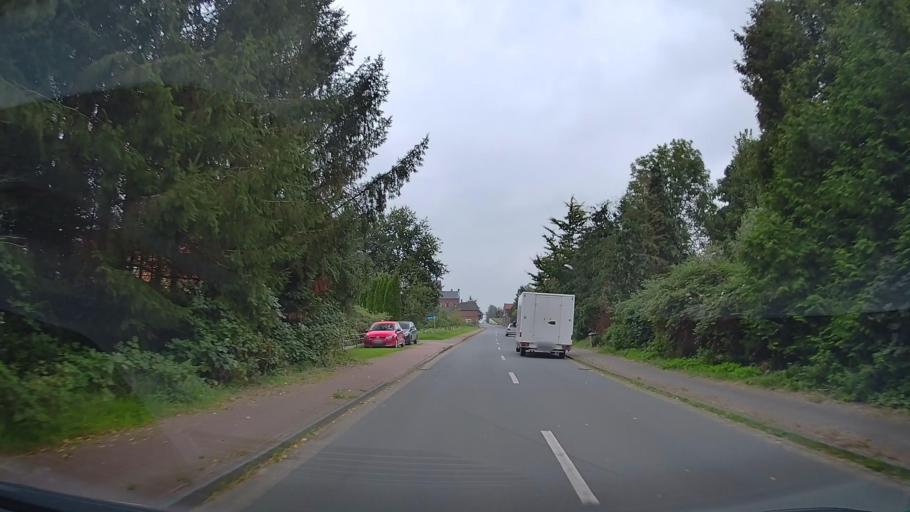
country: DE
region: Lower Saxony
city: Balje
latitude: 53.8298
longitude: 9.1333
